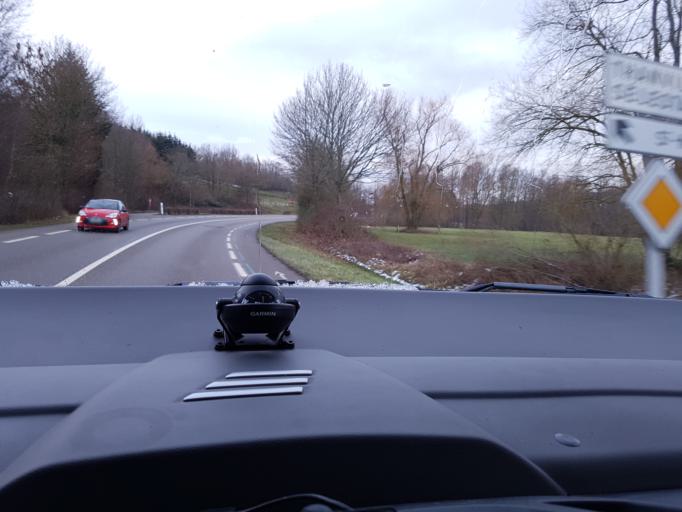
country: FR
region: Alsace
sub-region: Departement du Bas-Rhin
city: Ville
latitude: 48.3329
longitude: 7.3294
